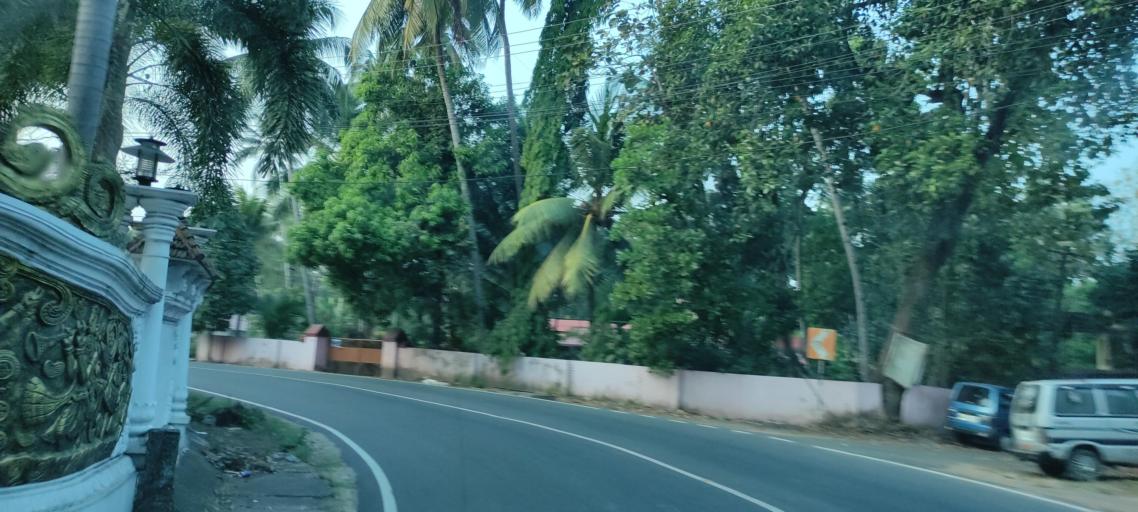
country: IN
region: Kerala
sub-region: Alappuzha
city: Mavelikara
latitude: 9.2710
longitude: 76.5385
